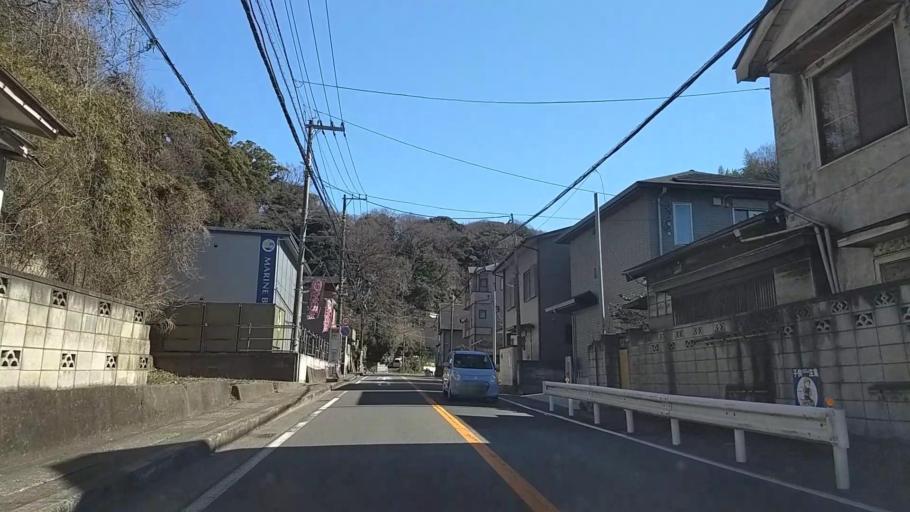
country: JP
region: Kanagawa
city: Kamakura
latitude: 35.3196
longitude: 139.5291
